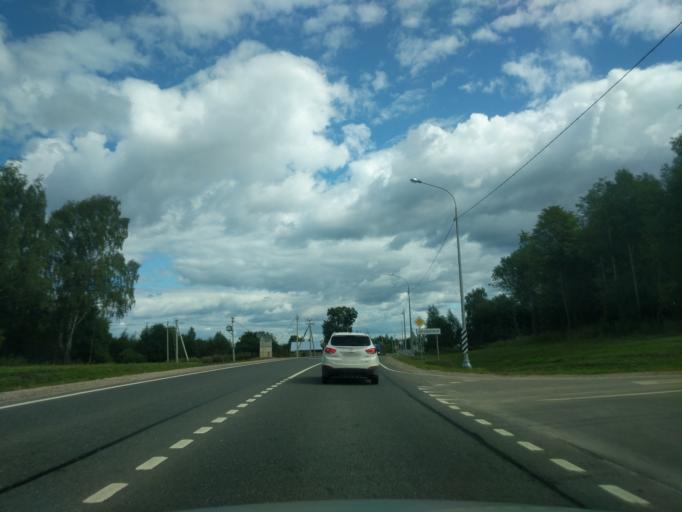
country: RU
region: Kostroma
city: Oktyabr'skiy
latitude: 57.7988
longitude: 41.1963
